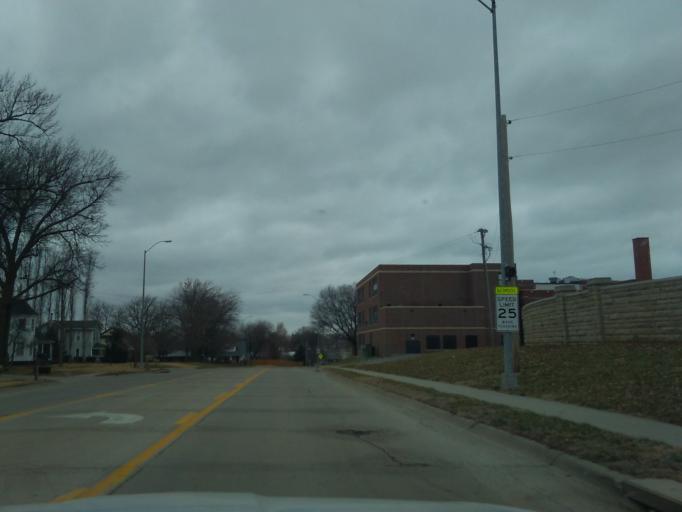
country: US
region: Nebraska
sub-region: Richardson County
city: Falls City
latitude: 40.0584
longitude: -95.5935
